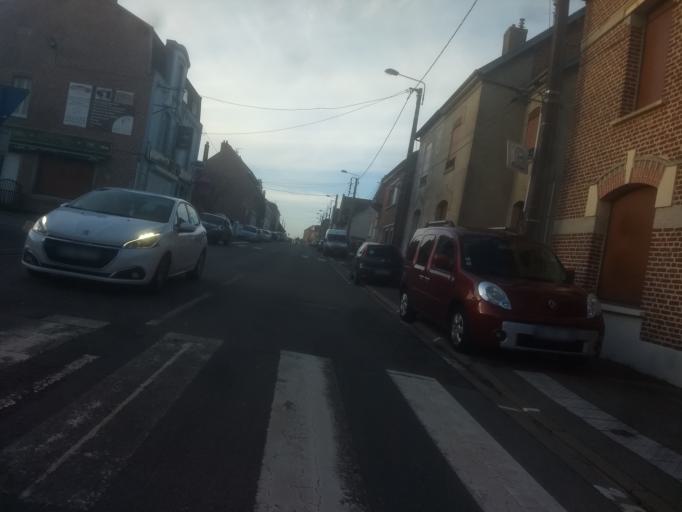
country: FR
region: Nord-Pas-de-Calais
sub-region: Departement du Pas-de-Calais
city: Beaurains
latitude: 50.2642
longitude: 2.7869
